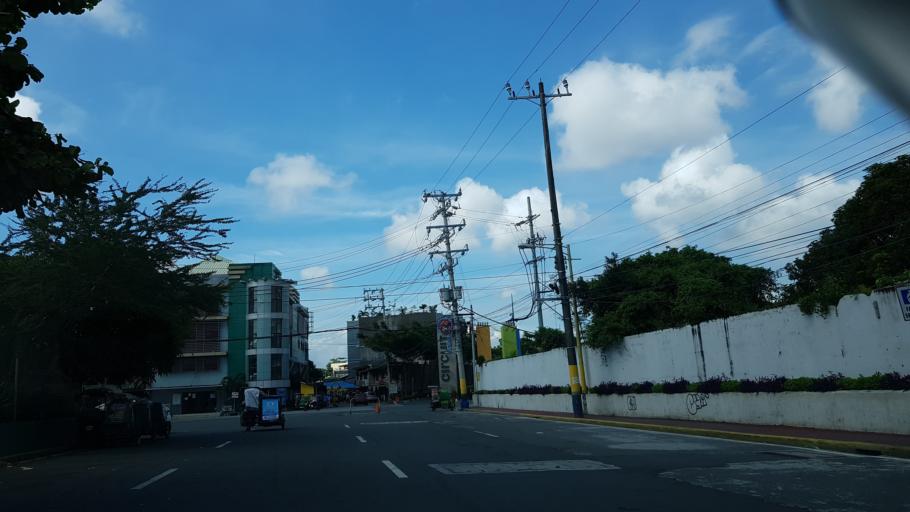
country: PH
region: Metro Manila
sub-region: Mandaluyong
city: Mandaluyong City
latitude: 14.5746
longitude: 121.0165
